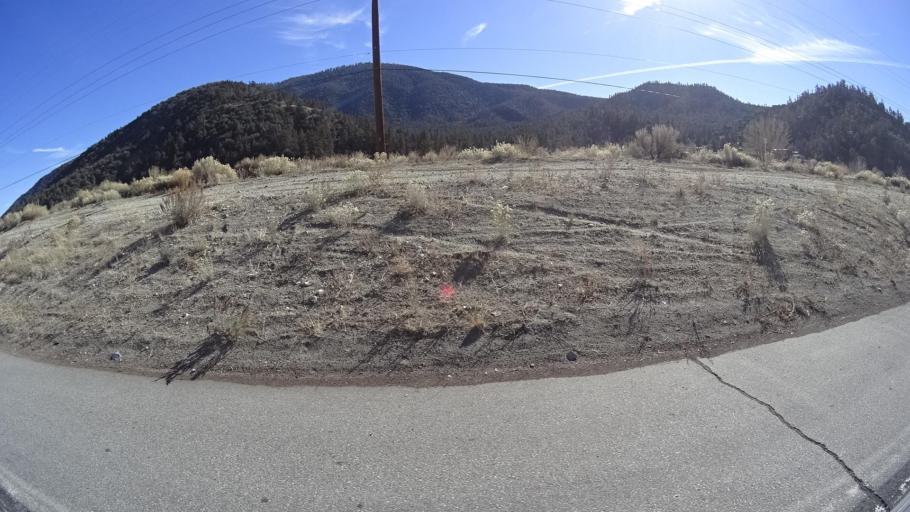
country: US
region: California
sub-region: Kern County
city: Frazier Park
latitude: 34.8196
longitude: -118.9903
